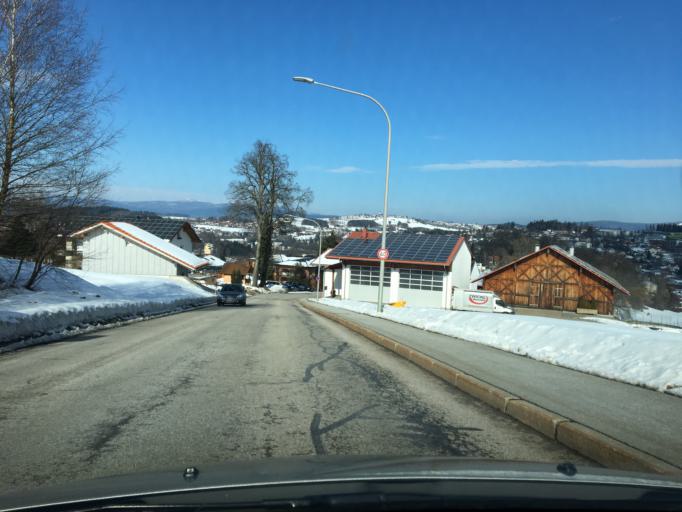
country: DE
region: Bavaria
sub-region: Lower Bavaria
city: Freyung
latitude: 48.7987
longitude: 13.5429
